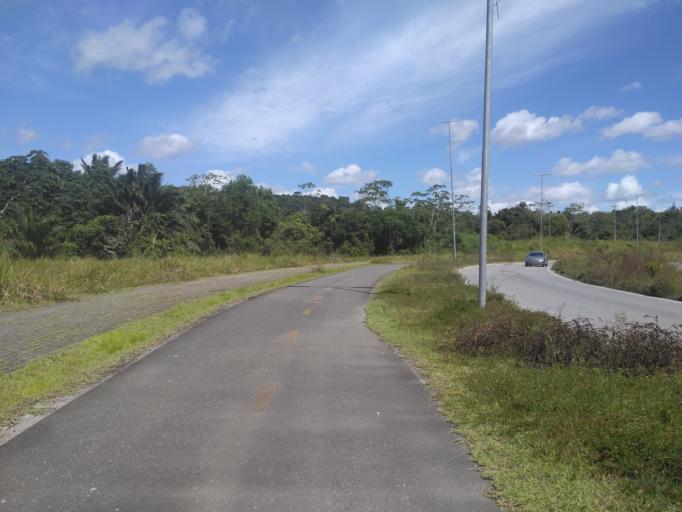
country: BR
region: Pernambuco
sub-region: Sao Lourenco Da Mata
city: Sao Lourenco da Mata
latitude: -8.0440
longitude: -34.9981
